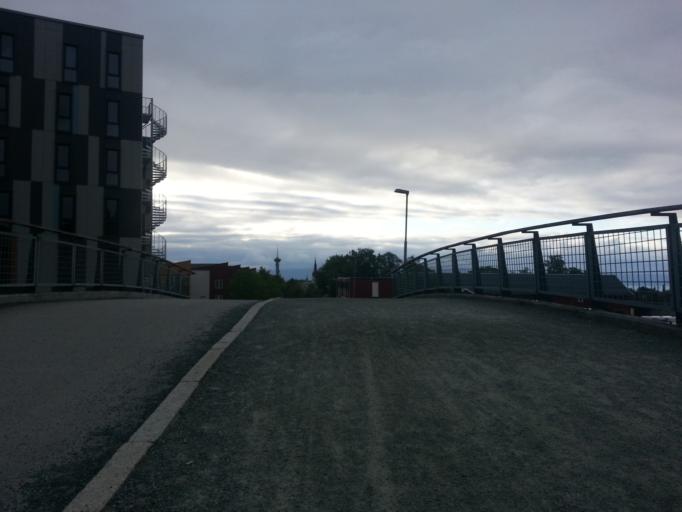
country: NO
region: Sor-Trondelag
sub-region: Trondheim
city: Trondheim
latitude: 63.4091
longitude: 10.4488
